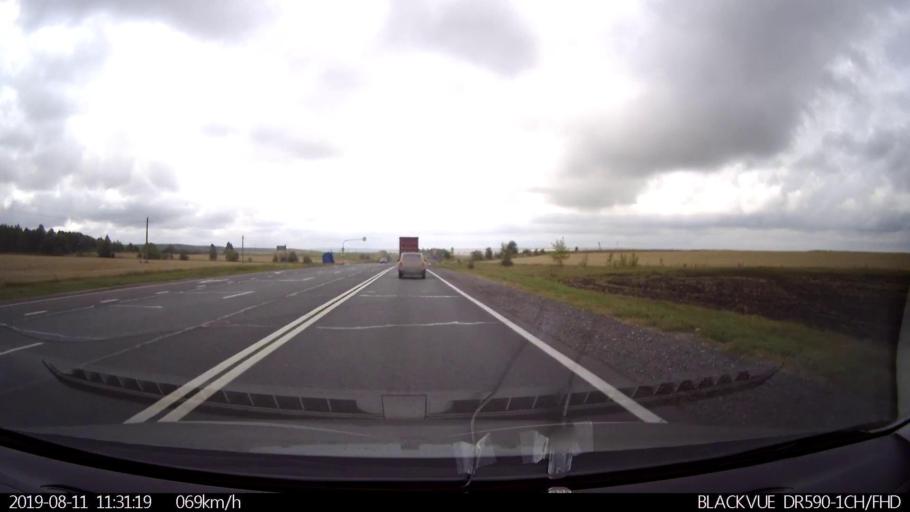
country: RU
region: Ulyanovsk
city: Krasnyy Gulyay
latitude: 54.0486
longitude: 48.2162
